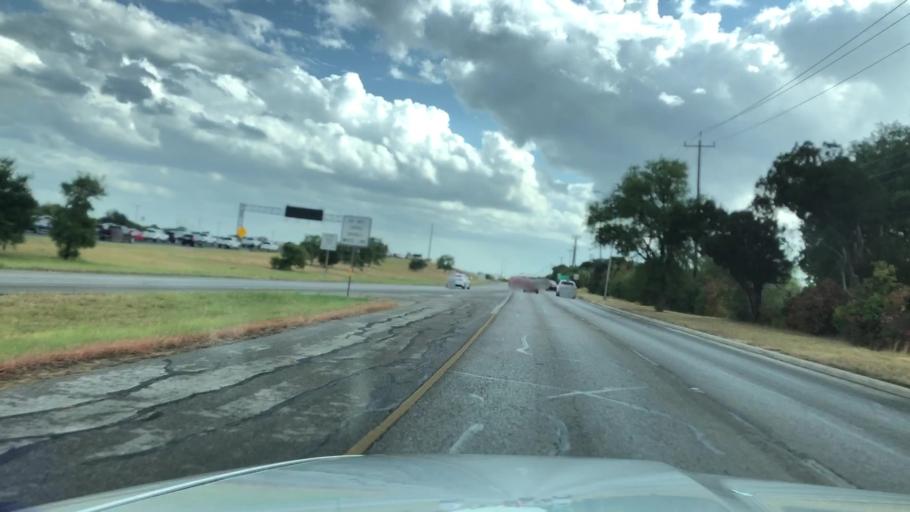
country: US
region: Texas
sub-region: Bexar County
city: Helotes
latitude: 29.5808
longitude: -98.6427
